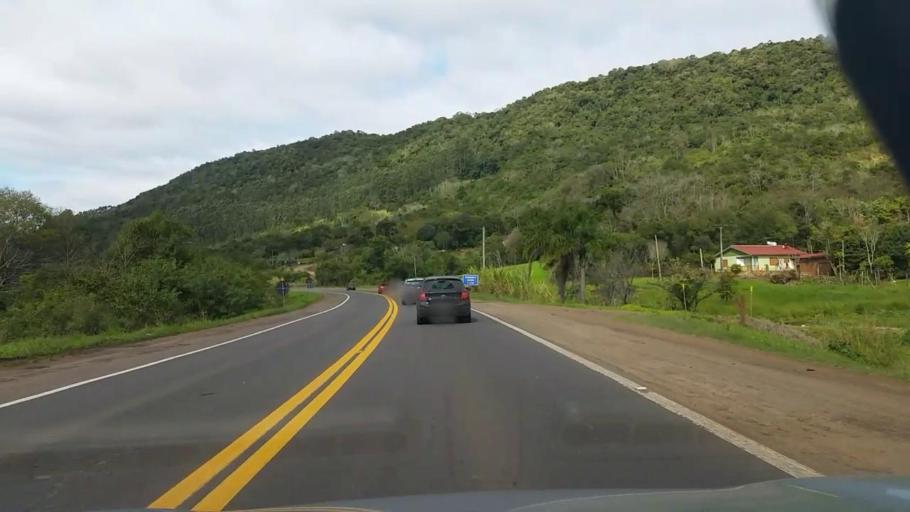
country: BR
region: Rio Grande do Sul
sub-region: Arroio Do Meio
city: Arroio do Meio
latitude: -29.3311
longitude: -52.1010
